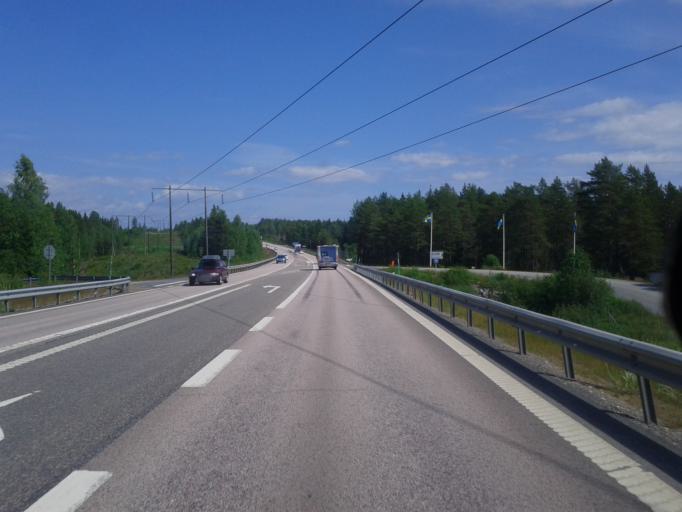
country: SE
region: Vaesternorrland
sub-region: OErnskoeldsviks Kommun
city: Husum
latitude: 63.4607
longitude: 19.2589
